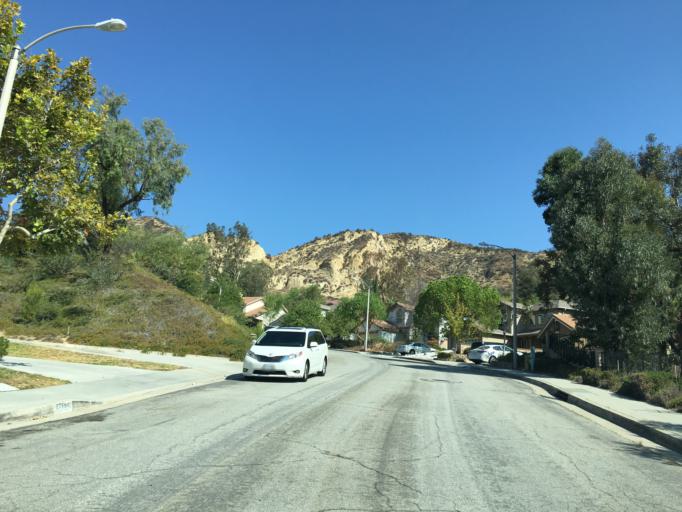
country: US
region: California
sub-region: Los Angeles County
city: Castaic
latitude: 34.4734
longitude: -118.6206
